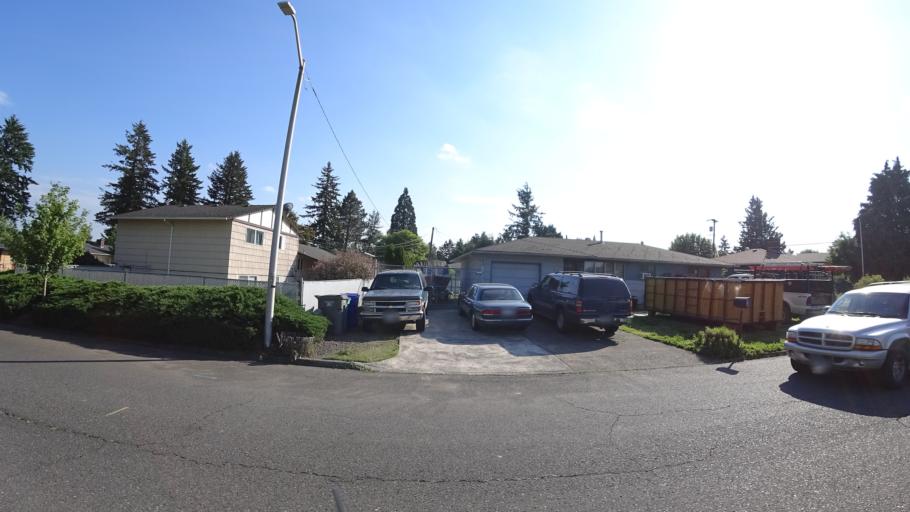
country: US
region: Oregon
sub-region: Multnomah County
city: Lents
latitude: 45.5136
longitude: -122.5065
